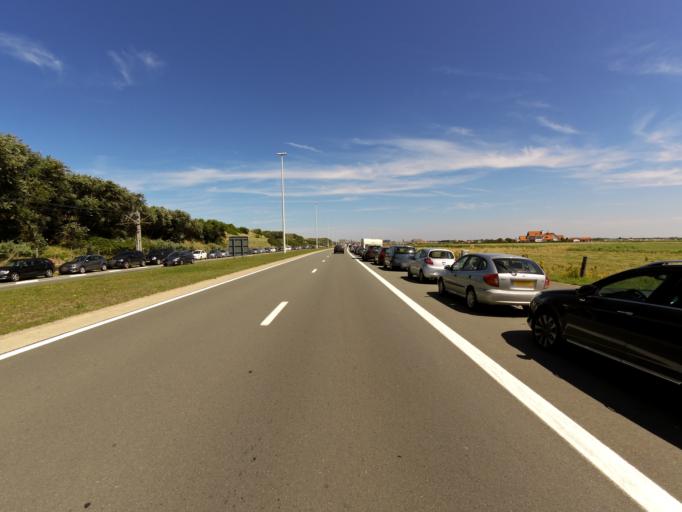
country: BE
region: Flanders
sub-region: Provincie West-Vlaanderen
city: Wenduine
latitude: 51.3040
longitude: 3.0883
